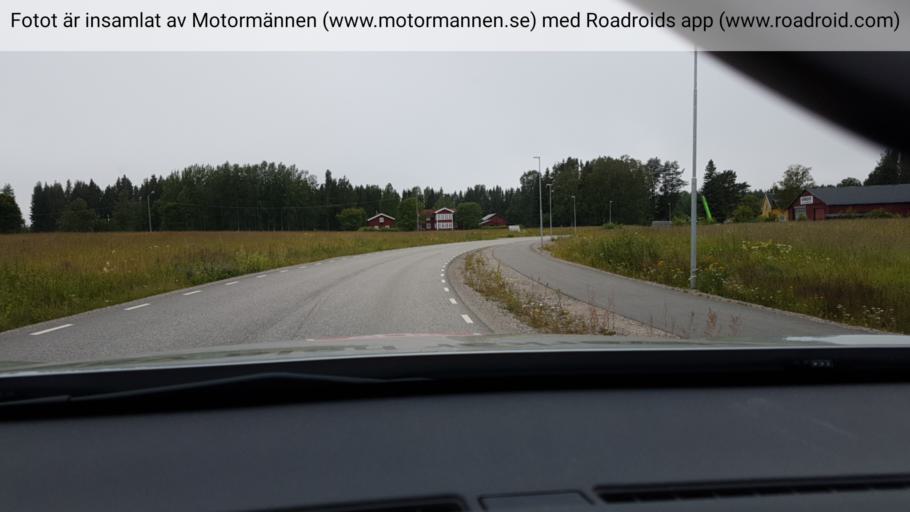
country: SE
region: Vaesternorrland
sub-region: Sundsvalls Kommun
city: Johannedal
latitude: 62.4289
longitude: 17.4473
